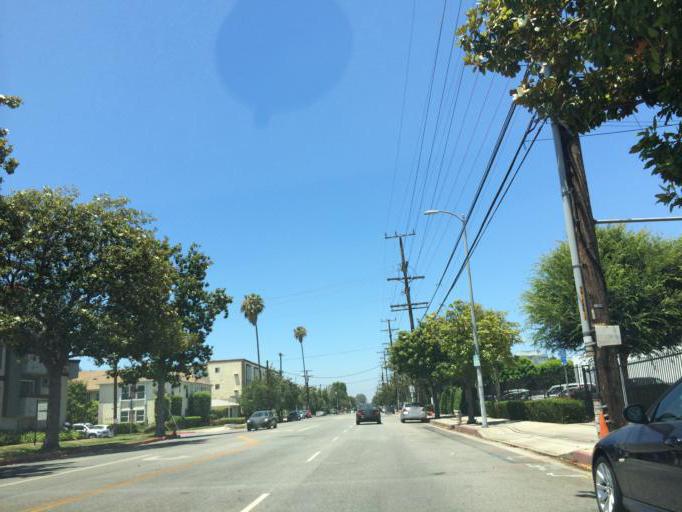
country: US
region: California
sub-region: Los Angeles County
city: Sherman Oaks
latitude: 34.1649
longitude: -118.4491
